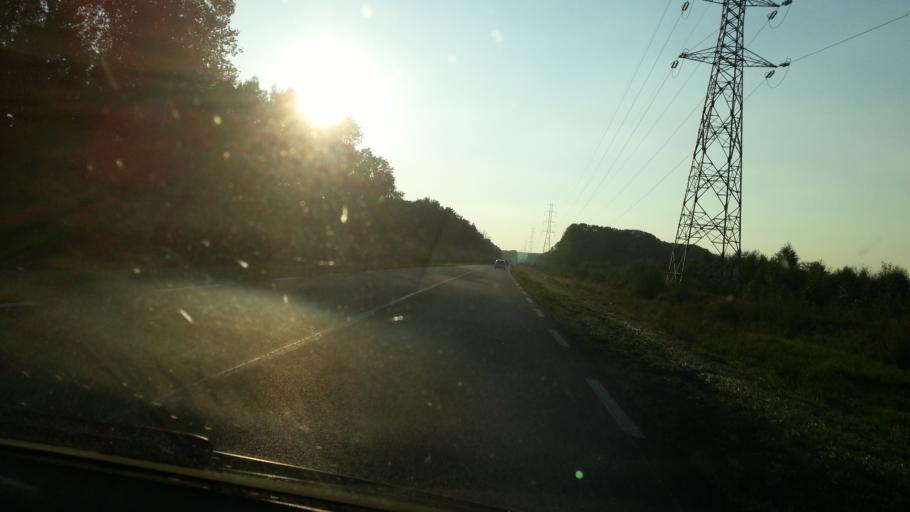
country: FR
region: Picardie
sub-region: Departement de l'Oise
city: Les Ageux
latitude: 49.3192
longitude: 2.5855
